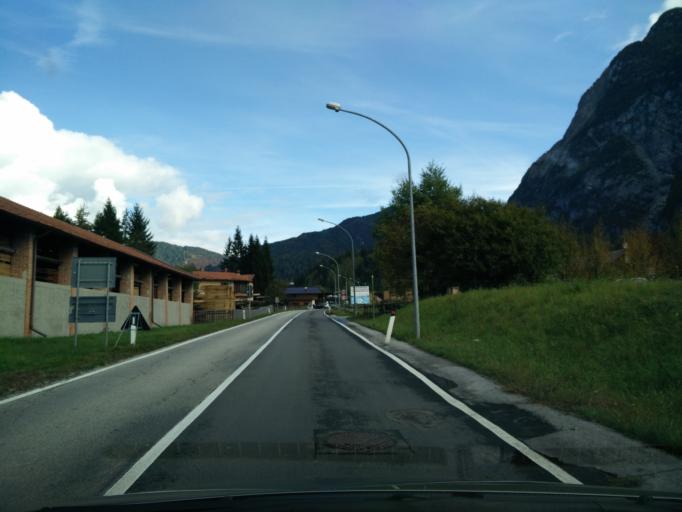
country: IT
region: Veneto
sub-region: Provincia di Belluno
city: Vigo di Cadore
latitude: 46.5123
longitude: 12.4618
